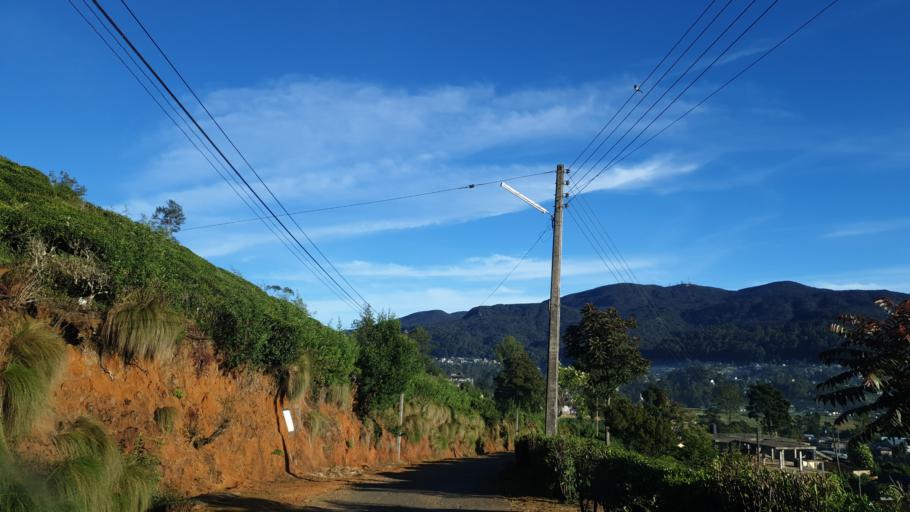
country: LK
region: Central
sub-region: Nuwara Eliya District
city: Nuwara Eliya
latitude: 6.9556
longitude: 80.7666
